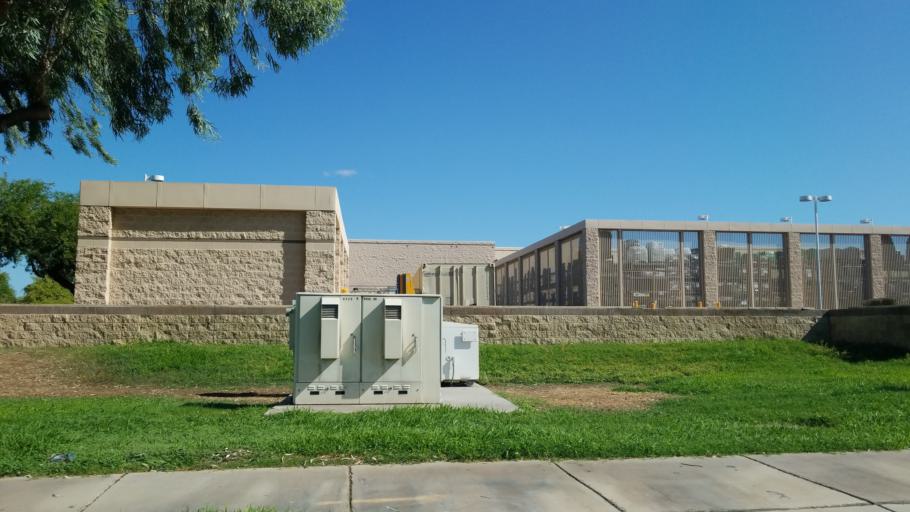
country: US
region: Arizona
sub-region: Maricopa County
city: Peoria
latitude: 33.6384
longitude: -112.2070
